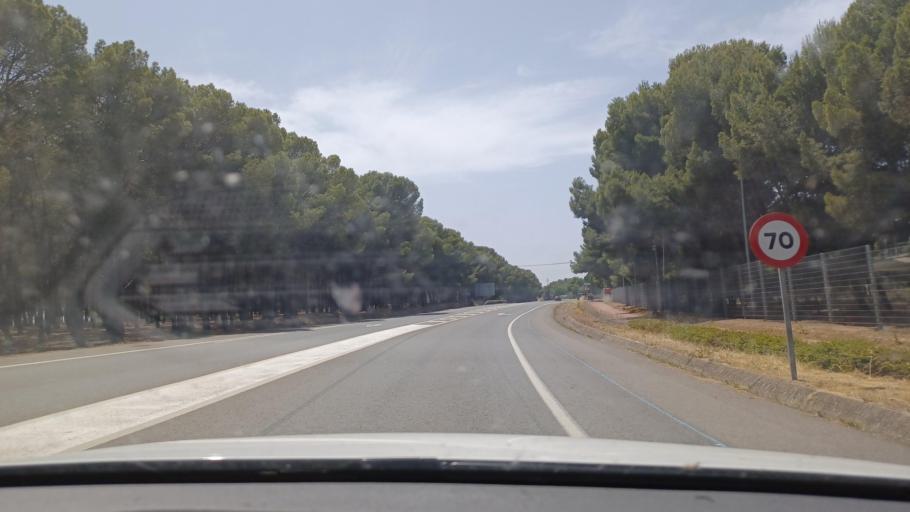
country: ES
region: Navarre
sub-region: Provincia de Navarra
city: Tudela
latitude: 42.0419
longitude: -1.6201
